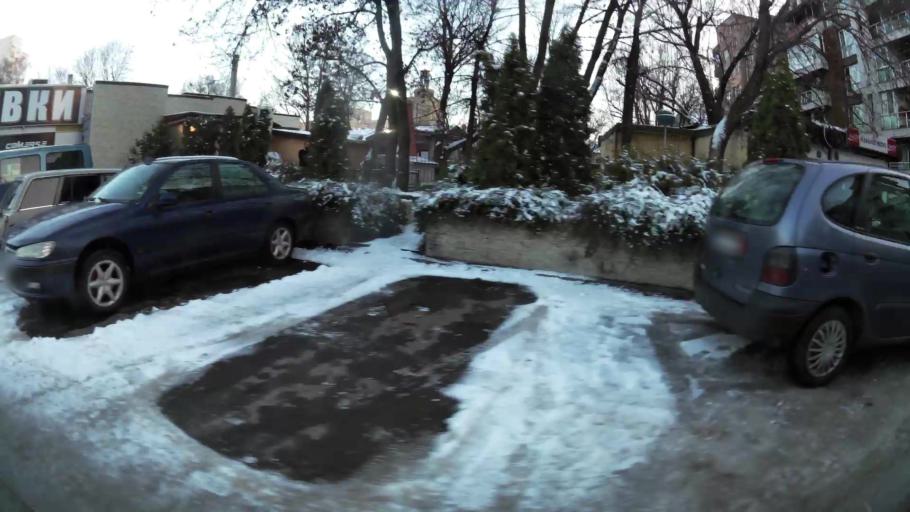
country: BG
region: Sofia-Capital
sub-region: Stolichna Obshtina
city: Sofia
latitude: 42.6811
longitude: 23.3736
